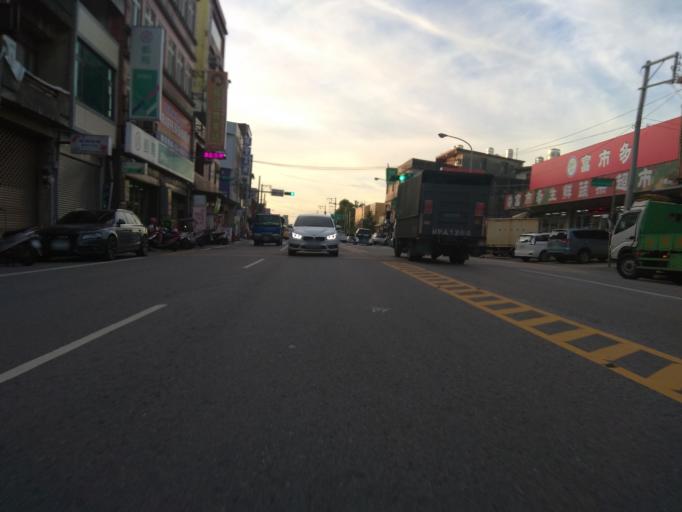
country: TW
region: Taiwan
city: Taoyuan City
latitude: 24.9885
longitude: 121.1807
